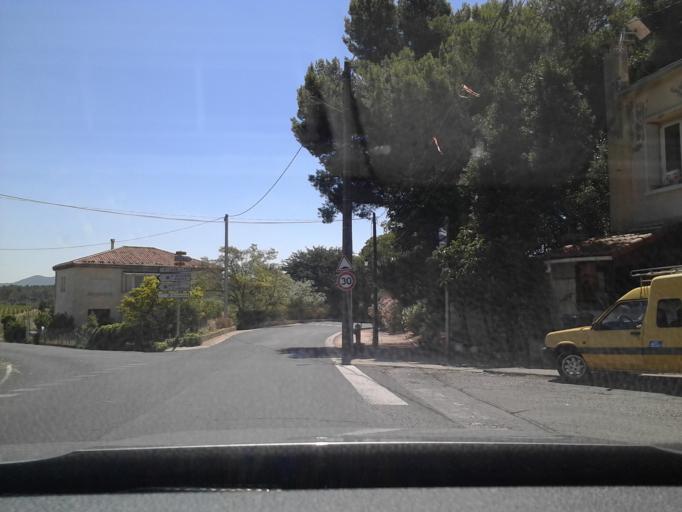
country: FR
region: Languedoc-Roussillon
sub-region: Departement de l'Herault
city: Montpeyroux
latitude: 43.6937
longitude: 3.5093
